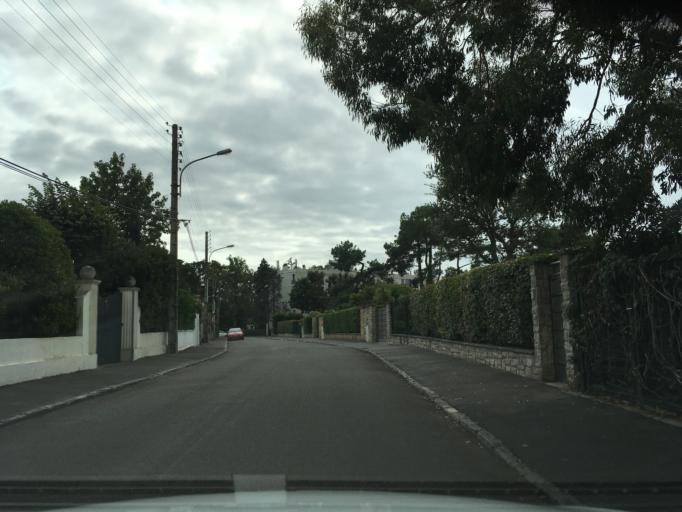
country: FR
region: Aquitaine
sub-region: Departement des Pyrenees-Atlantiques
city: Biarritz
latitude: 43.4772
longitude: -1.5418
